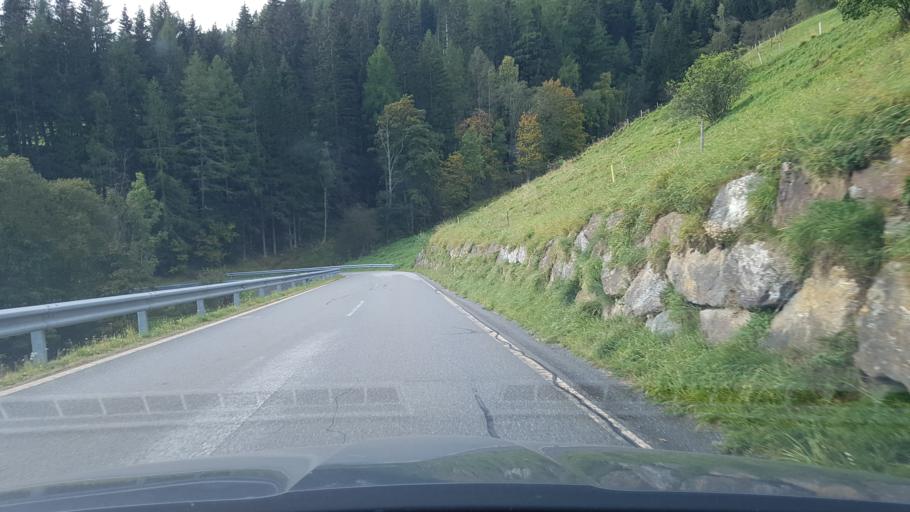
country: AT
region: Styria
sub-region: Politischer Bezirk Murau
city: Schoder
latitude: 47.1991
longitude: 14.1142
